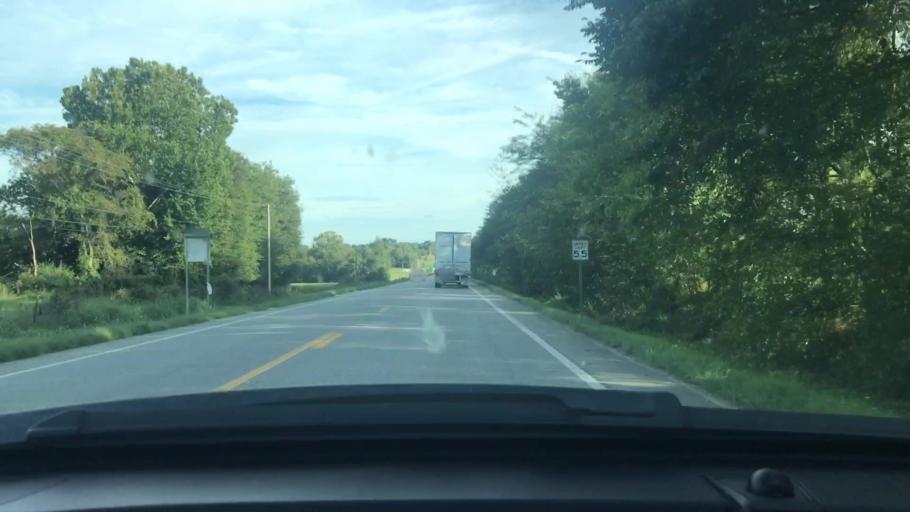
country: US
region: Arkansas
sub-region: Randolph County
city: Pocahontas
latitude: 36.1961
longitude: -91.1678
